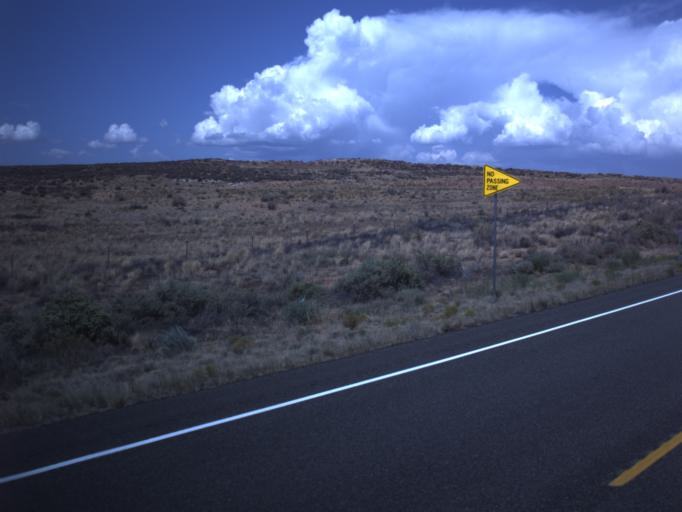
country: US
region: Utah
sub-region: San Juan County
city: Blanding
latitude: 37.3329
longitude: -109.5196
